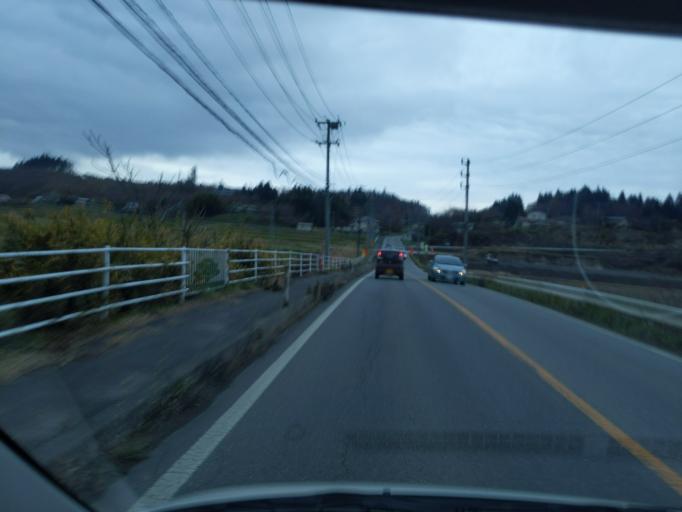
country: JP
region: Iwate
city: Ichinoseki
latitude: 39.0204
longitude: 141.3304
